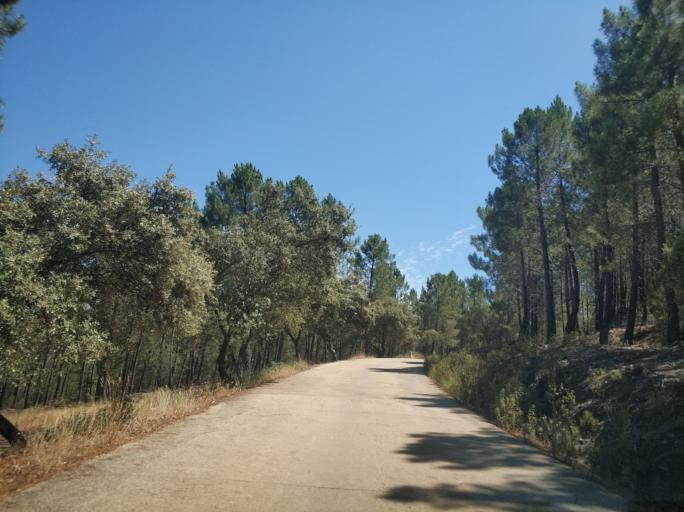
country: ES
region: Castille and Leon
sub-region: Provincia de Salamanca
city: Herguijuela de la Sierra
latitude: 40.3987
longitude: -6.0754
